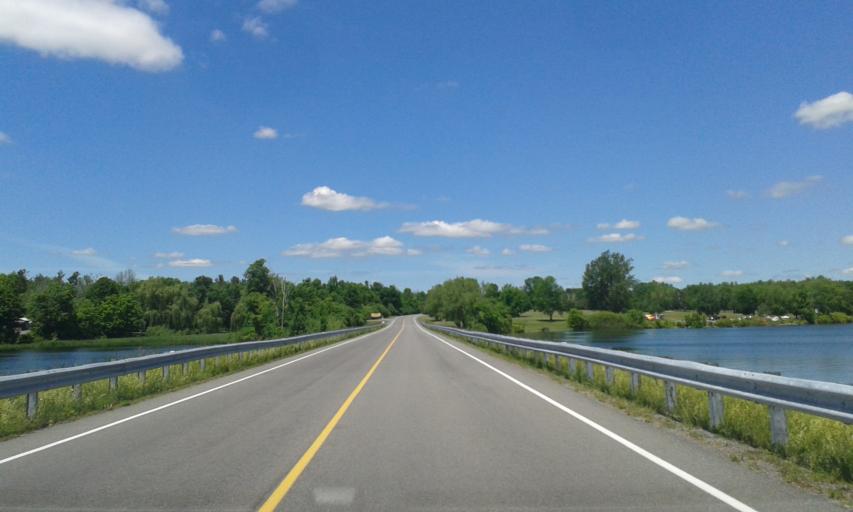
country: US
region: New York
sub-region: St. Lawrence County
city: Massena
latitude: 45.0089
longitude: -74.8950
